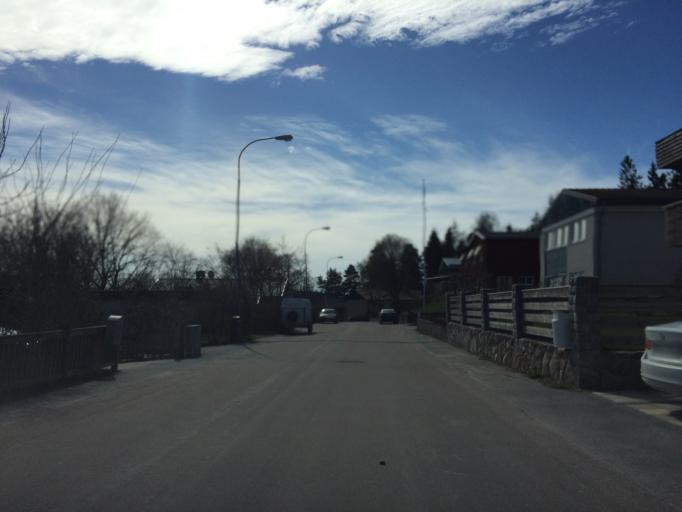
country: SE
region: Stockholm
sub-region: Sollentuna Kommun
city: Sollentuna
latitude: 59.4521
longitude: 17.9139
